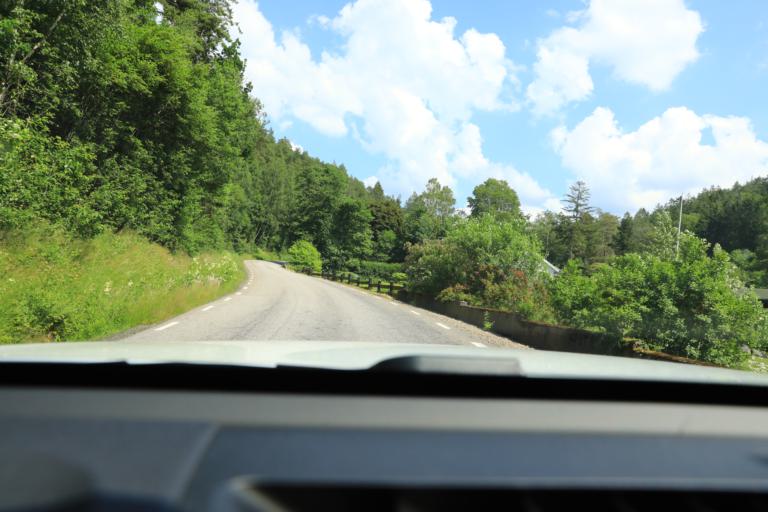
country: SE
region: Halland
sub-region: Varbergs Kommun
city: Veddige
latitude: 57.2042
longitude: 12.3359
